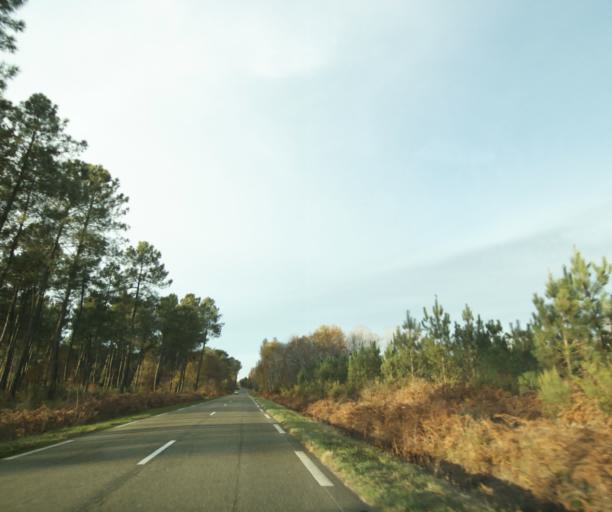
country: FR
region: Aquitaine
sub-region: Departement des Landes
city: Gabarret
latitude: 44.0313
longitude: -0.0297
